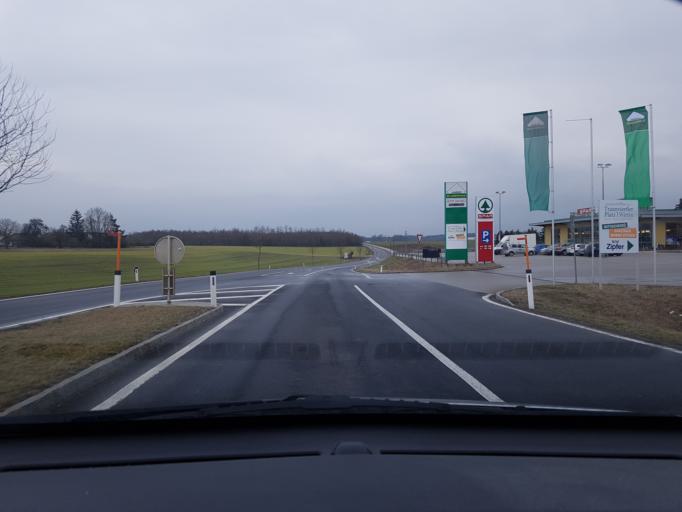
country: AT
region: Upper Austria
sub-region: Steyr Stadt
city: Steyr
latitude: 48.0872
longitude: 14.3702
